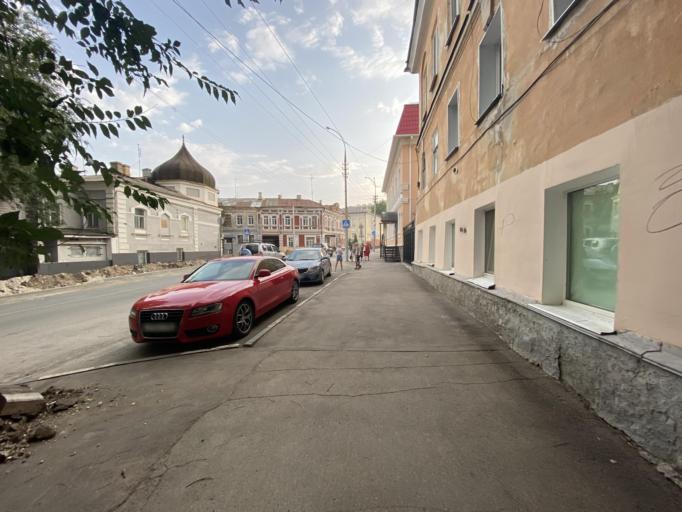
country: RU
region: Saratov
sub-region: Saratovskiy Rayon
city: Saratov
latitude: 51.5284
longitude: 46.0579
